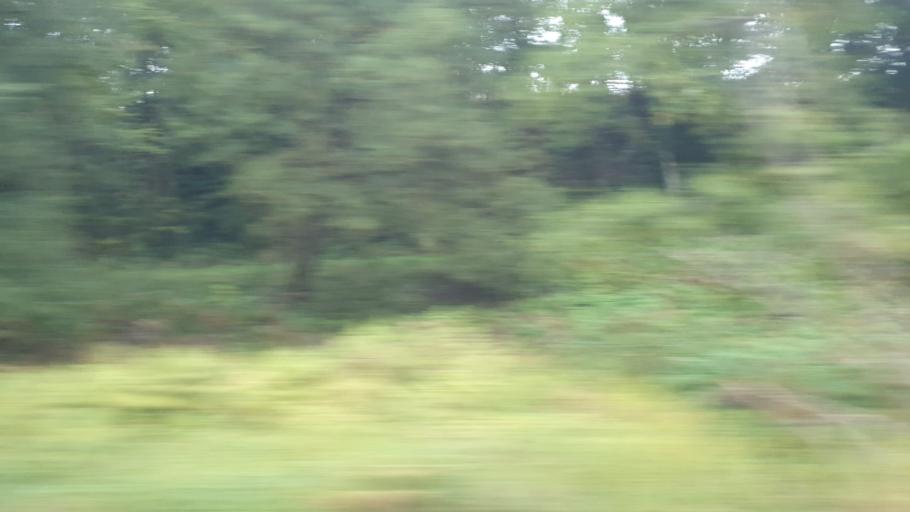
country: DE
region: Saarland
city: Blieskastel
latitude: 49.2505
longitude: 7.2403
